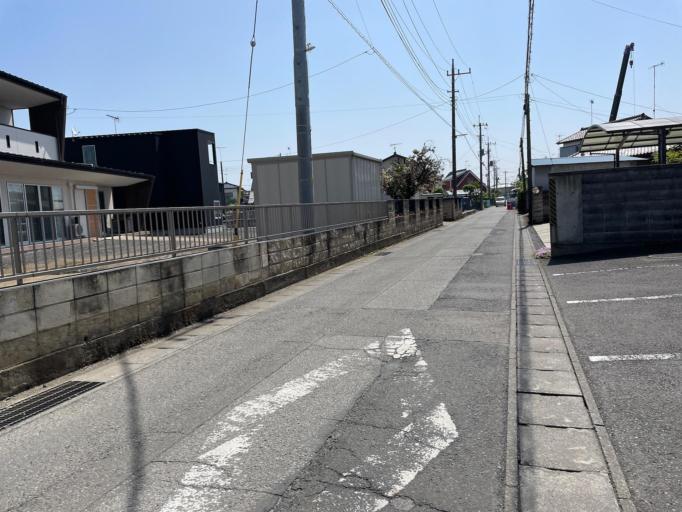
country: JP
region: Gunma
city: Ota
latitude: 36.3019
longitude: 139.4063
